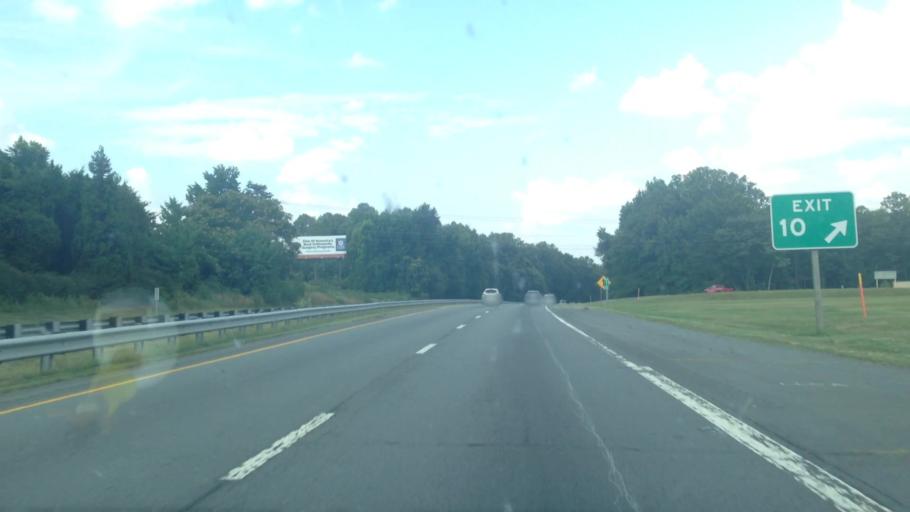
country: US
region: North Carolina
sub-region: Forsyth County
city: Walkertown
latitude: 36.1117
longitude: -80.1640
